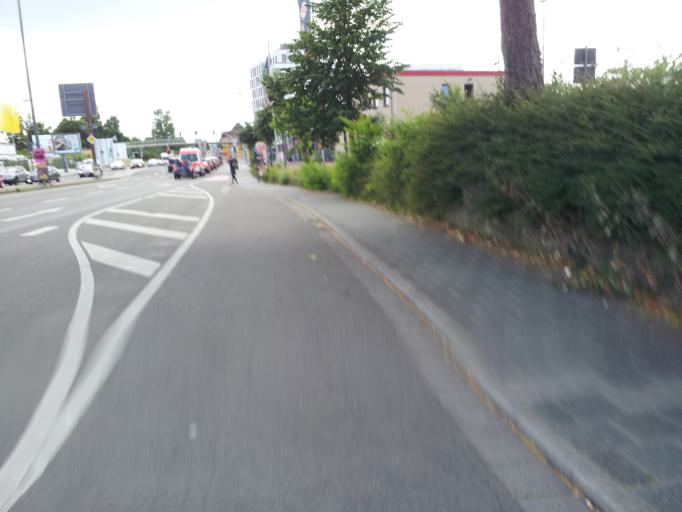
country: DE
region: Baden-Wuerttemberg
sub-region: Karlsruhe Region
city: Heidelberg
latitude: 49.3989
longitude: 8.6752
